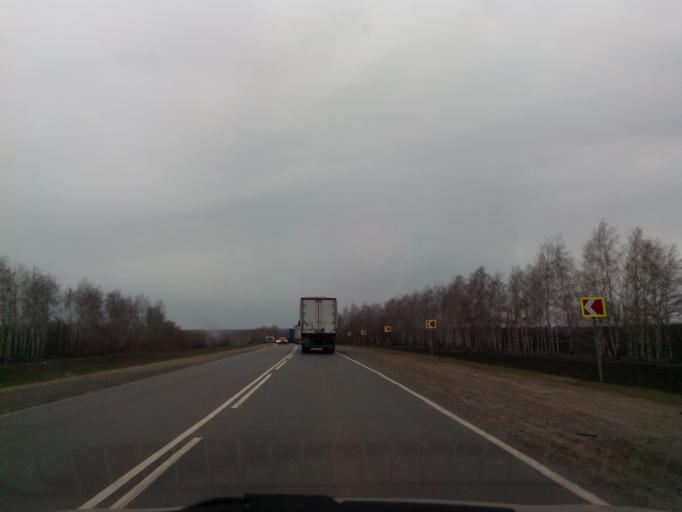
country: RU
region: Tambov
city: Pokrovo-Prigorodnoye
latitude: 52.6692
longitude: 41.3372
